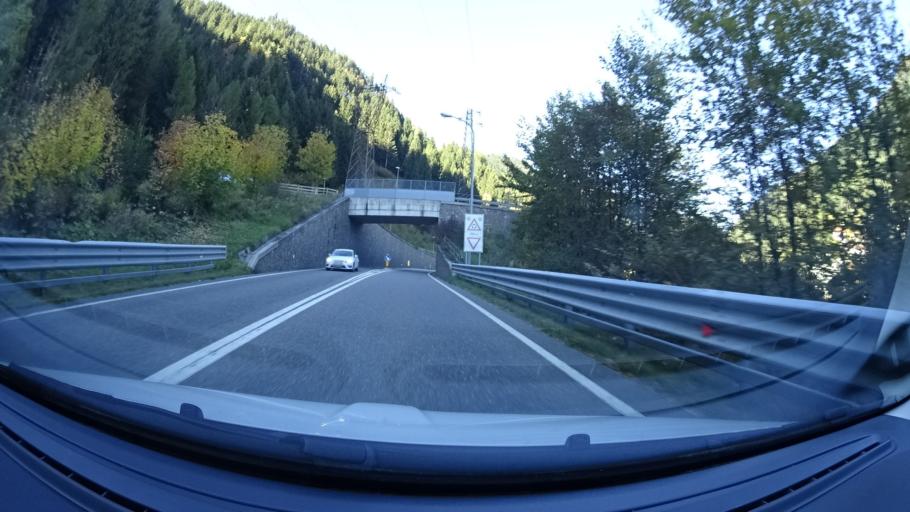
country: IT
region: Trentino-Alto Adige
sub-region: Provincia di Trento
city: Predazzo
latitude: 46.3179
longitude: 11.5950
